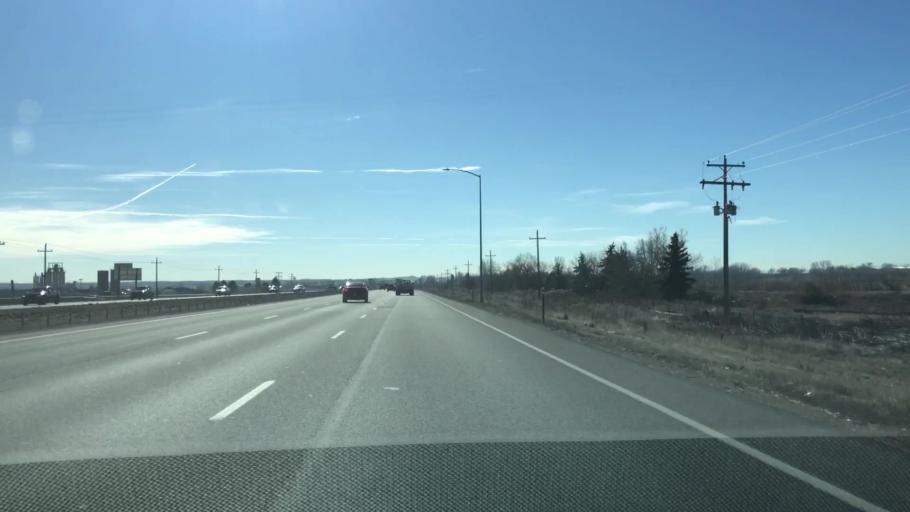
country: US
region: Colorado
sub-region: Weld County
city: Windsor
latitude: 40.5200
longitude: -104.9906
